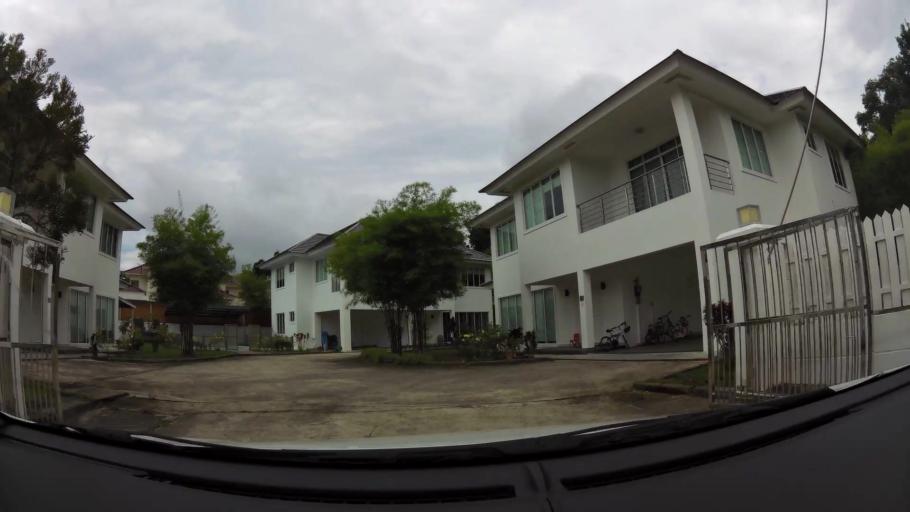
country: BN
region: Brunei and Muara
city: Bandar Seri Begawan
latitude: 4.8887
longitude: 114.9170
